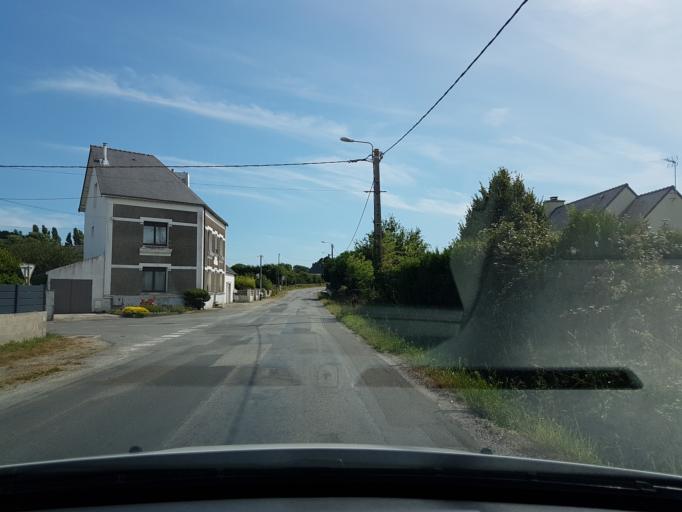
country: FR
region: Brittany
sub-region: Departement du Morbihan
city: Etel
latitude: 47.6747
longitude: -3.2205
